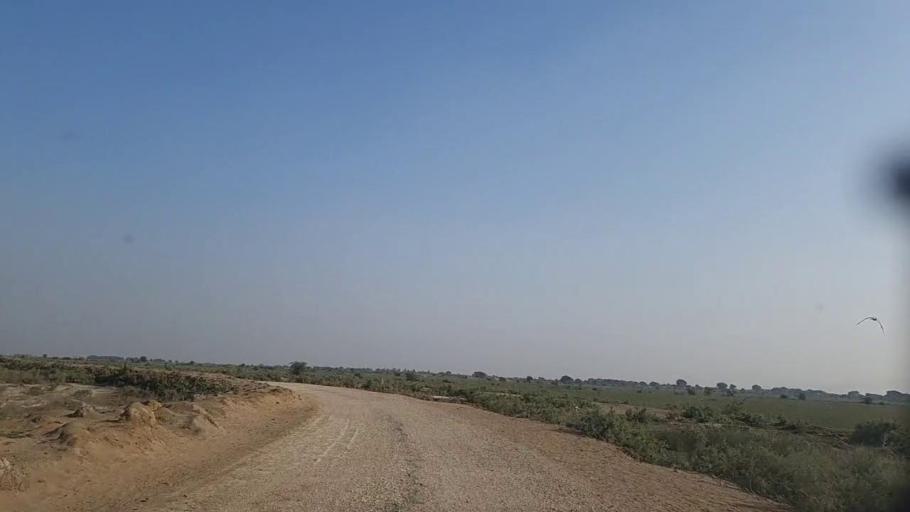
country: PK
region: Sindh
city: Jati
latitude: 24.4606
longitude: 68.2850
